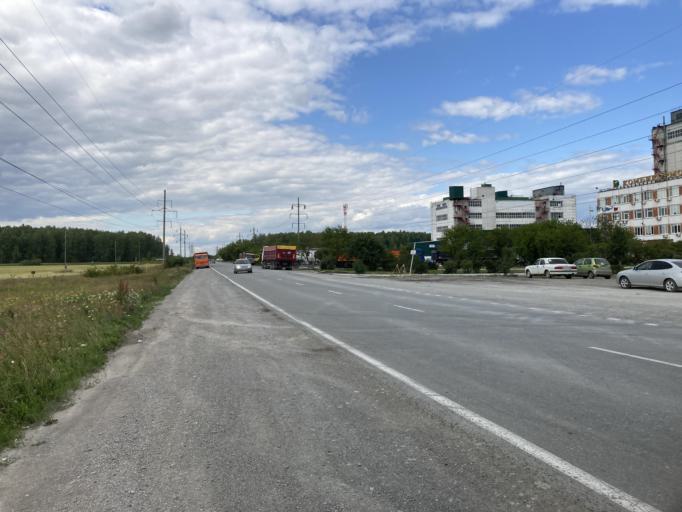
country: RU
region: Sverdlovsk
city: Bogdanovich
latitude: 56.8044
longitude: 62.0355
